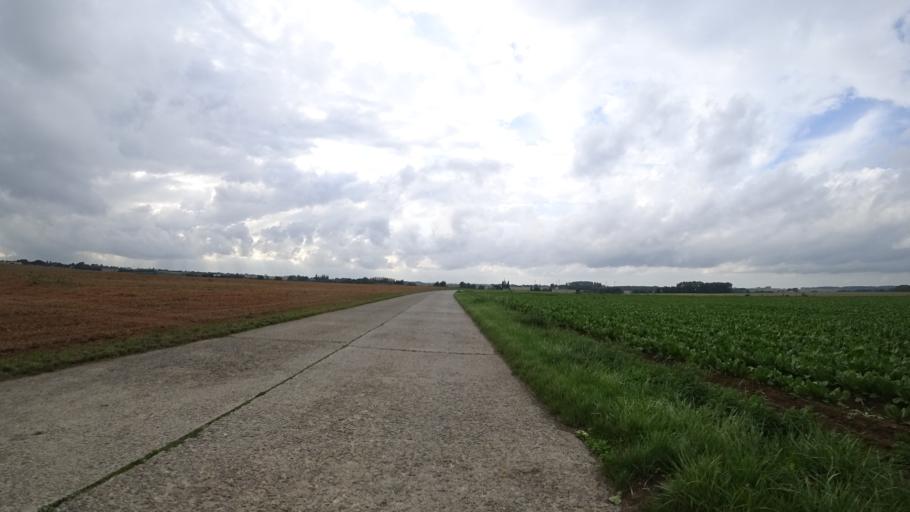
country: BE
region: Wallonia
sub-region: Province de Namur
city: Gembloux
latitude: 50.5638
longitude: 4.7444
